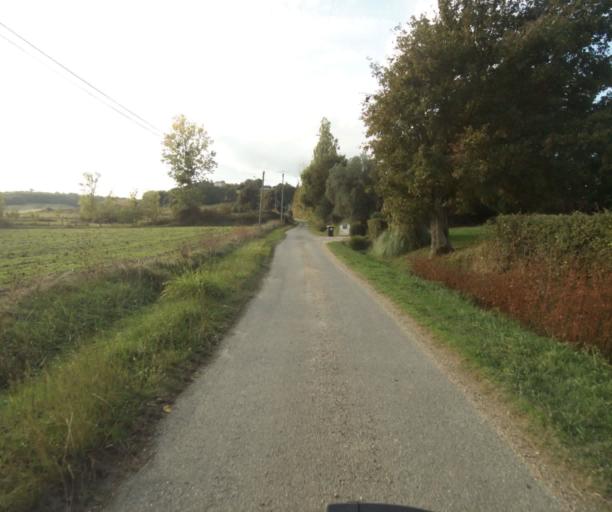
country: FR
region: Midi-Pyrenees
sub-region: Departement de la Haute-Garonne
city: Launac
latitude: 43.8186
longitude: 1.1231
